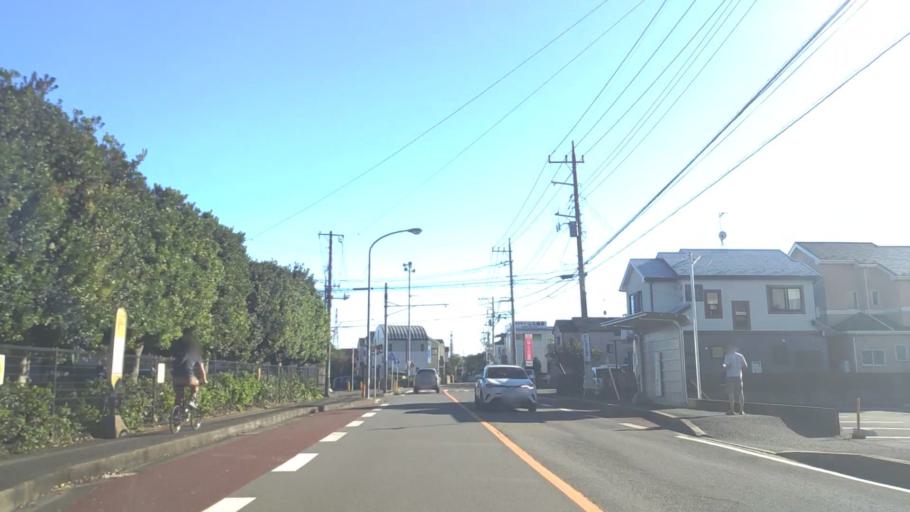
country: JP
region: Kanagawa
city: Atsugi
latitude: 35.4186
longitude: 139.3656
